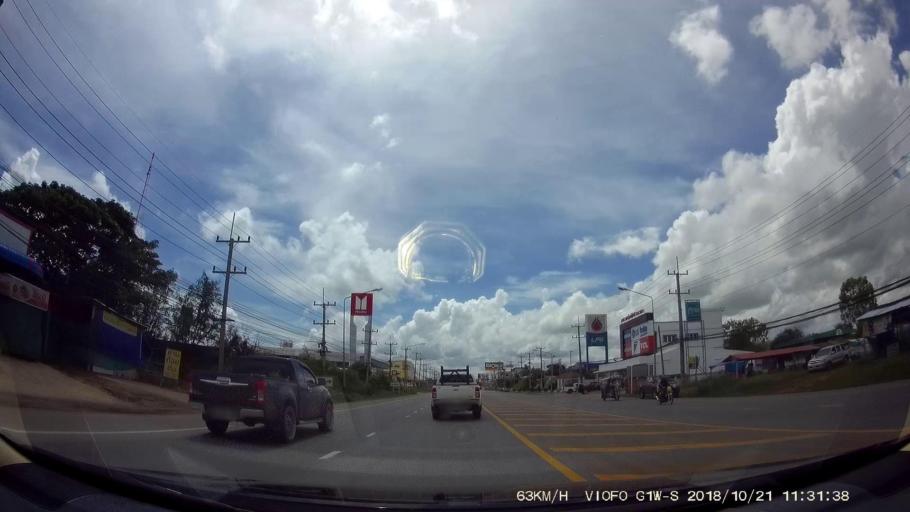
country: TH
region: Chaiyaphum
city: Chaiyaphum
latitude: 15.7675
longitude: 102.0254
